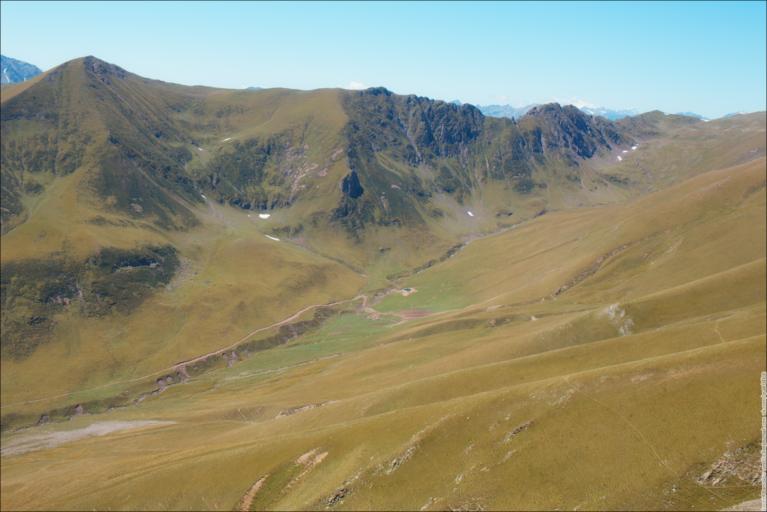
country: RU
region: Karachayevo-Cherkesiya
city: Mednogorskiy
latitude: 43.6138
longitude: 41.0943
